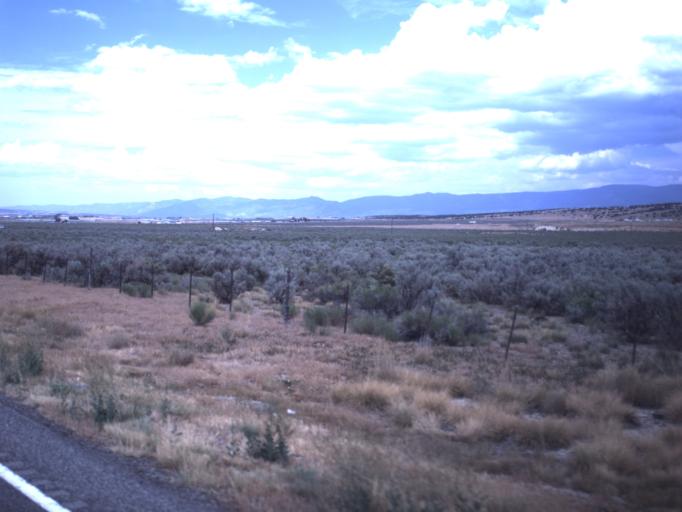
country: US
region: Utah
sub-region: Sanpete County
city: Ephraim
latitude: 39.4397
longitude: -111.5624
